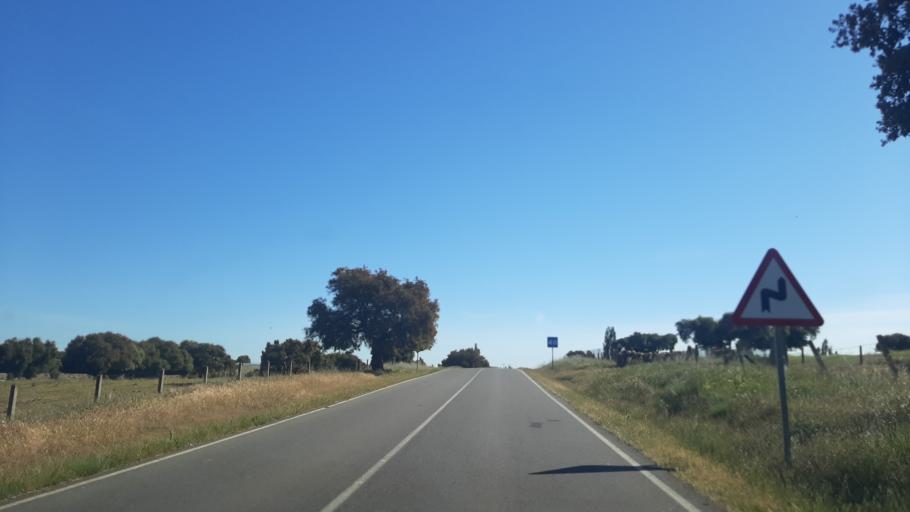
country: ES
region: Castille and Leon
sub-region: Provincia de Salamanca
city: Salvatierra de Tormes
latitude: 40.5556
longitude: -5.5866
